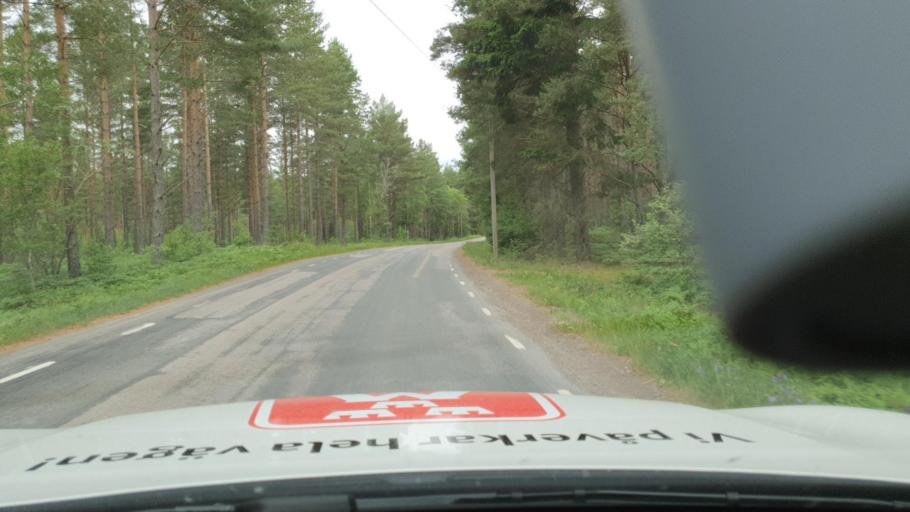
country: SE
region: Vaestra Goetaland
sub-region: Tidaholms Kommun
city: Olofstorp
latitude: 58.3205
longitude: 13.9994
